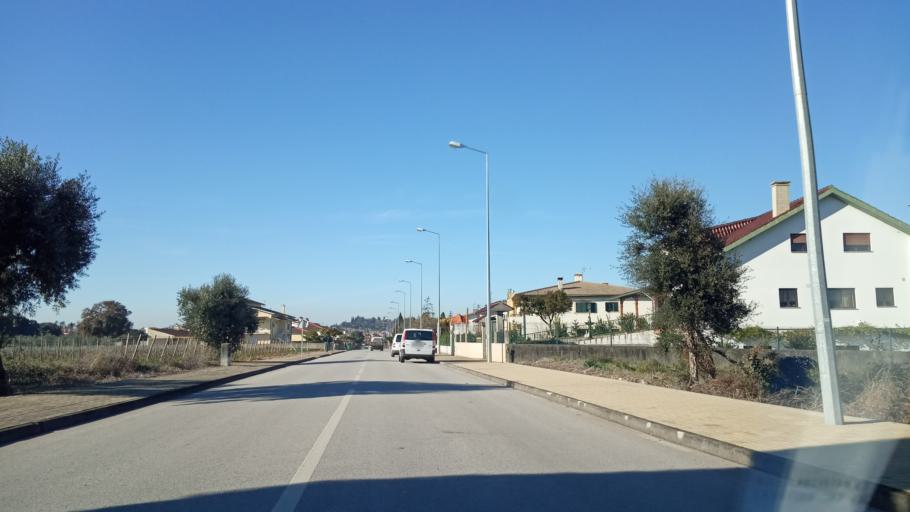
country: PT
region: Aveiro
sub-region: Anadia
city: Anadia
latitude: 40.4332
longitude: -8.4267
